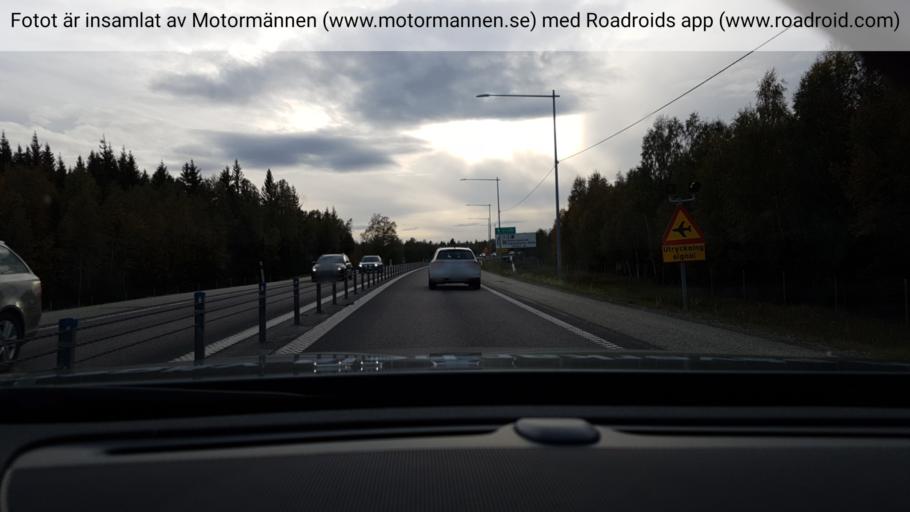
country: SE
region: Vaesternorrland
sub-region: Timra Kommun
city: Soraker
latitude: 62.5183
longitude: 17.4629
